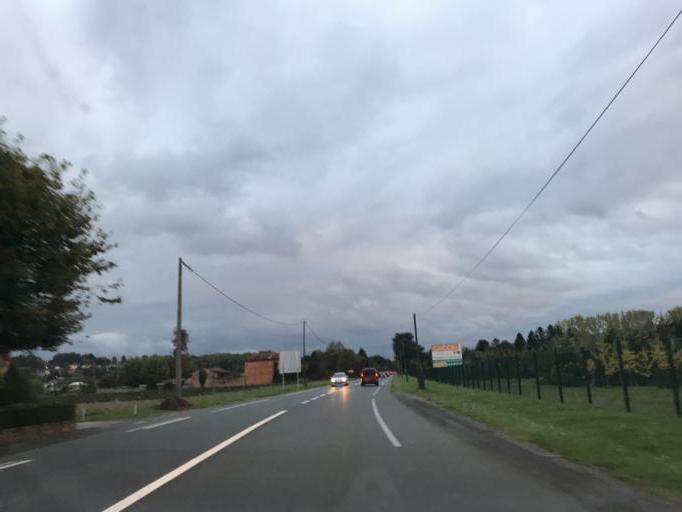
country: FR
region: Rhone-Alpes
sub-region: Departement de l'Ain
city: Reyrieux
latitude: 45.9204
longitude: 4.8142
